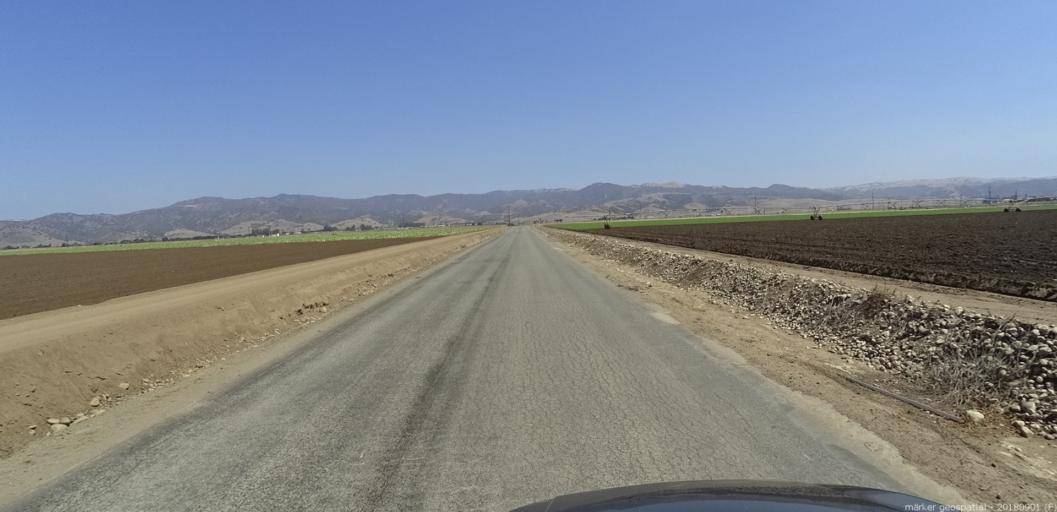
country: US
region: California
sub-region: Monterey County
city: Chualar
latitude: 36.5997
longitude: -121.5156
